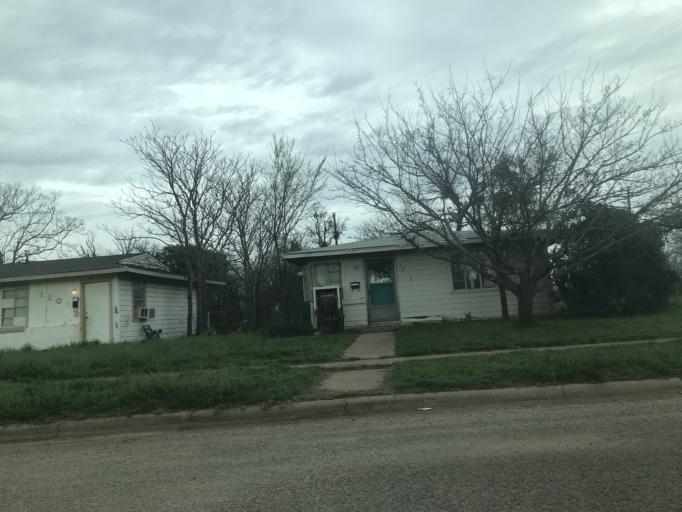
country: US
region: Texas
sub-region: Taylor County
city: Abilene
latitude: 32.4633
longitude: -99.7479
